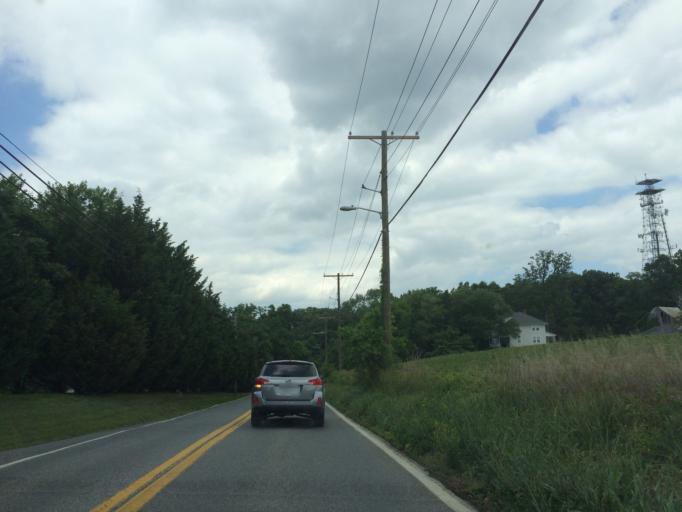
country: US
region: Maryland
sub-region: Baltimore County
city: Randallstown
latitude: 39.3505
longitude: -76.8016
